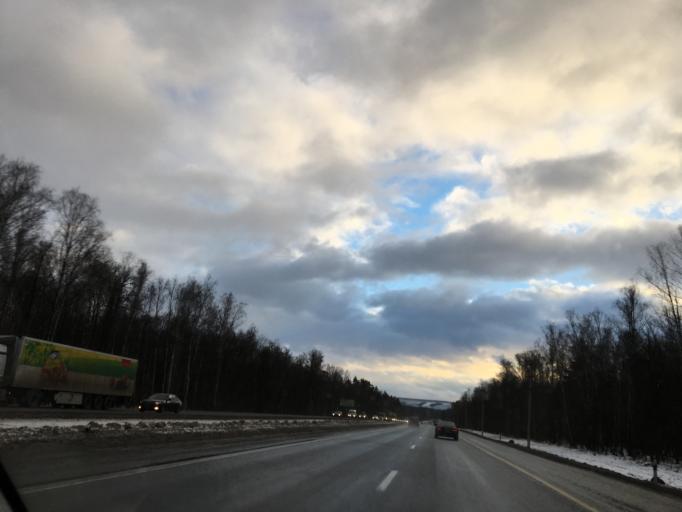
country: RU
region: Moskovskaya
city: Danki
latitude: 54.8979
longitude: 37.5116
